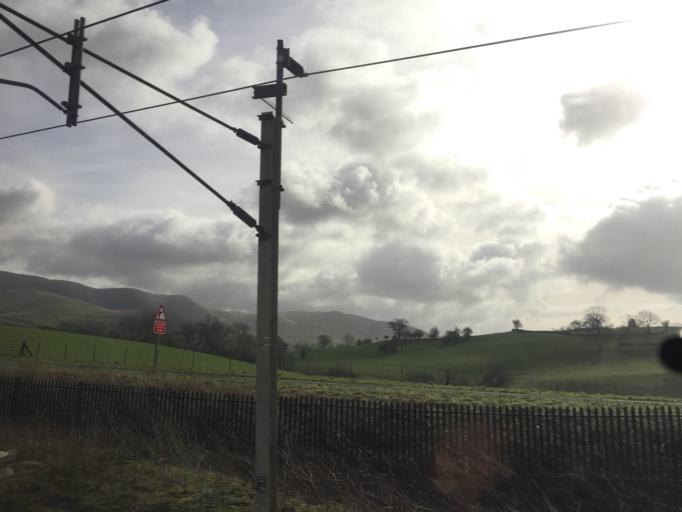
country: GB
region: England
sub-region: Cumbria
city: Sedbergh
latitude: 54.3611
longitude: -2.6032
